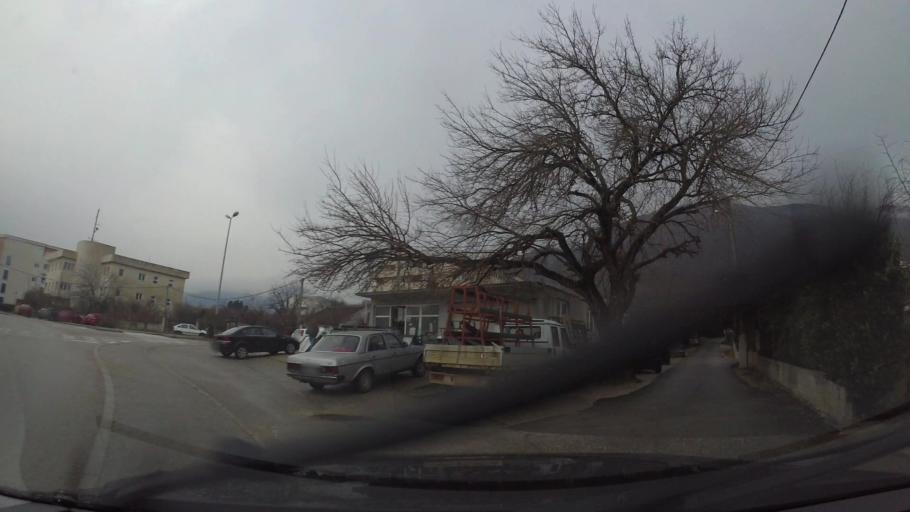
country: BA
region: Federation of Bosnia and Herzegovina
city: Cim
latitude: 43.3548
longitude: 17.7952
